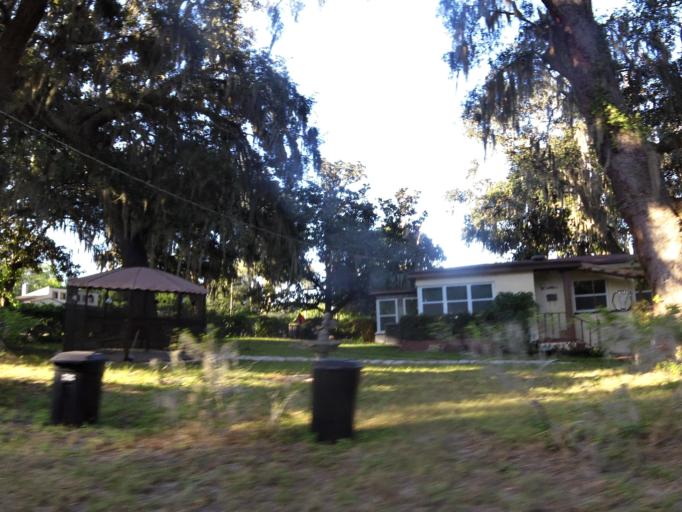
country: US
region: Florida
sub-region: Duval County
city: Jacksonville
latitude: 30.2644
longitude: -81.6424
